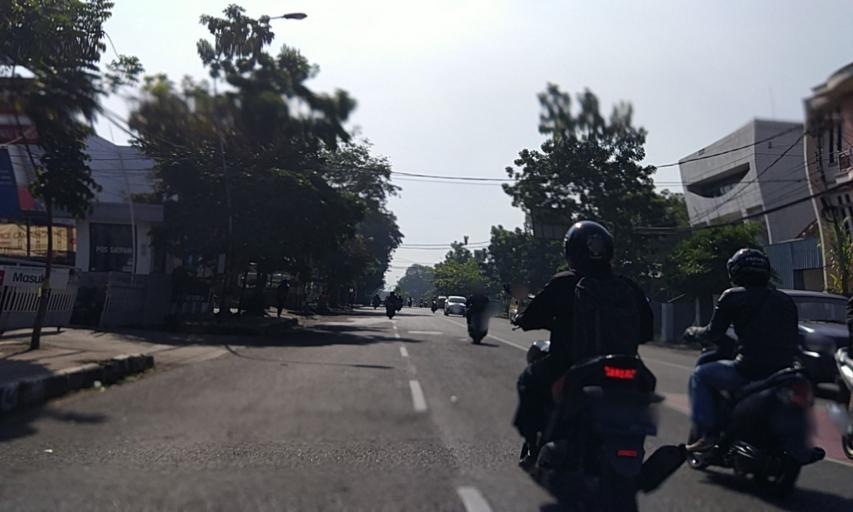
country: ID
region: West Java
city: Bandung
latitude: -6.9171
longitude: 107.6274
